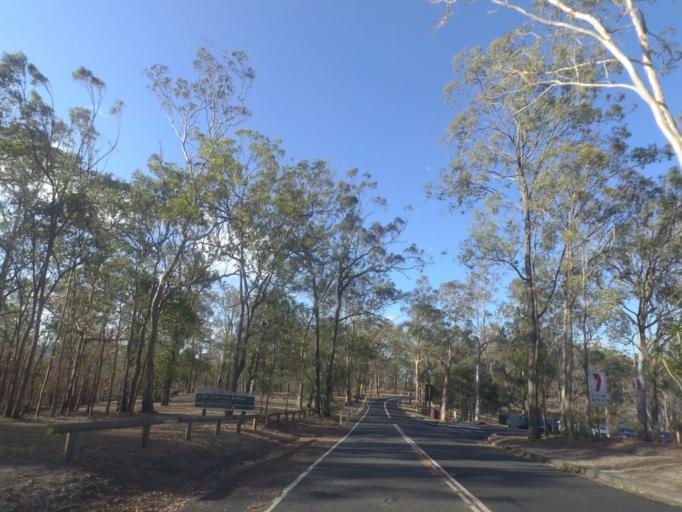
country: AU
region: Queensland
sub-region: Brisbane
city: Kenmore Hills
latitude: -27.4659
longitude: 152.9431
